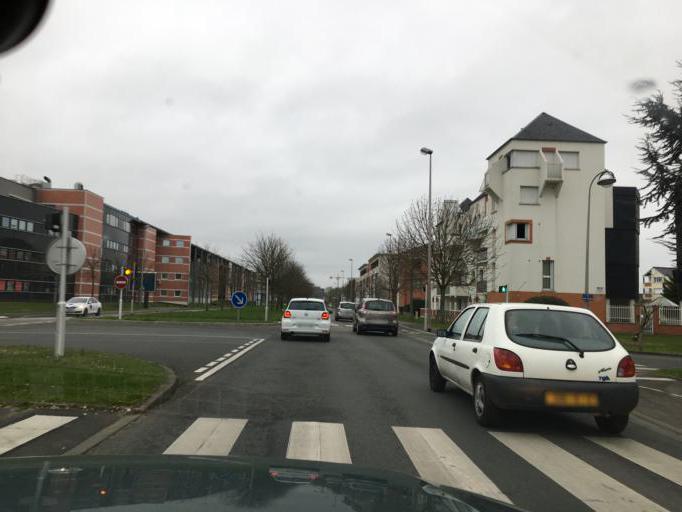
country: FR
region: Centre
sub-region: Departement du Loiret
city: Fleury-les-Aubrais
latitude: 47.9159
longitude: 1.9242
